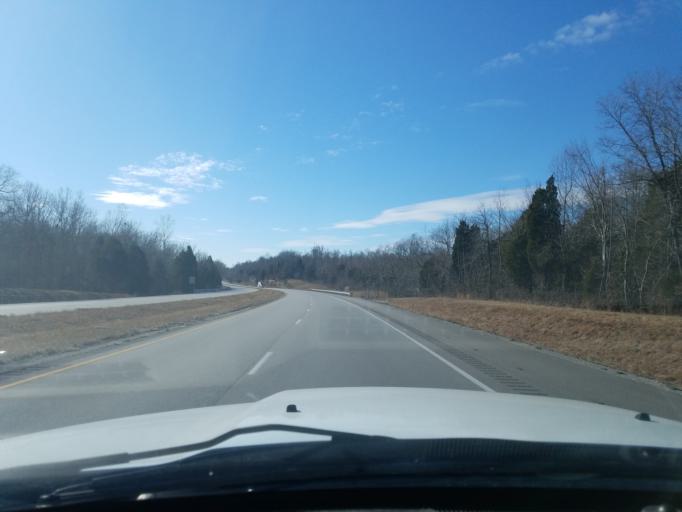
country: US
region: Kentucky
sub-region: Grayson County
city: Leitchfield
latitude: 37.5490
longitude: -86.1205
